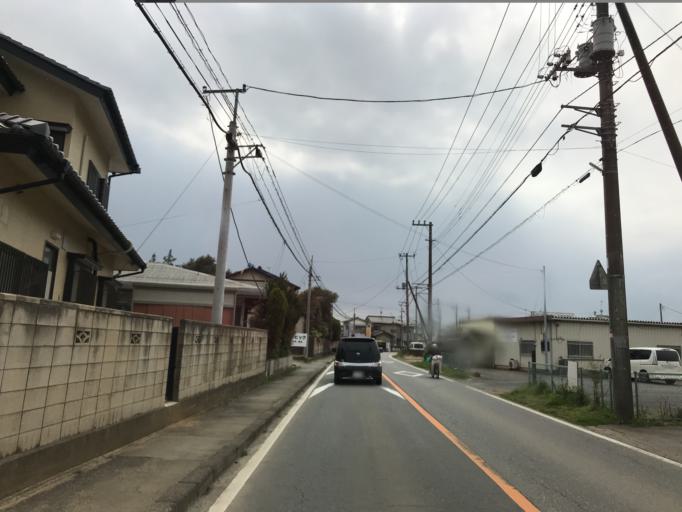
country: JP
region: Ibaraki
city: Moriya
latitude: 35.9851
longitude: 140.0571
